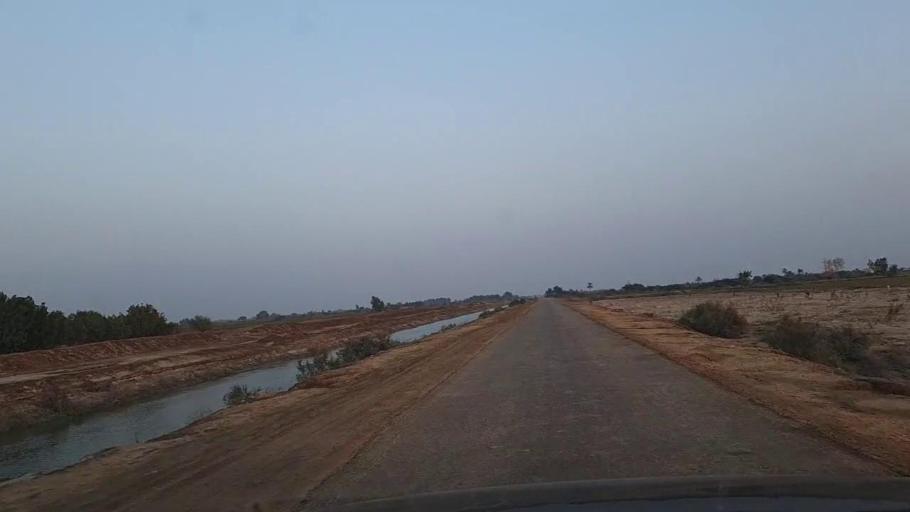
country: PK
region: Sindh
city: Mirpur Sakro
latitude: 24.6345
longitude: 67.6120
